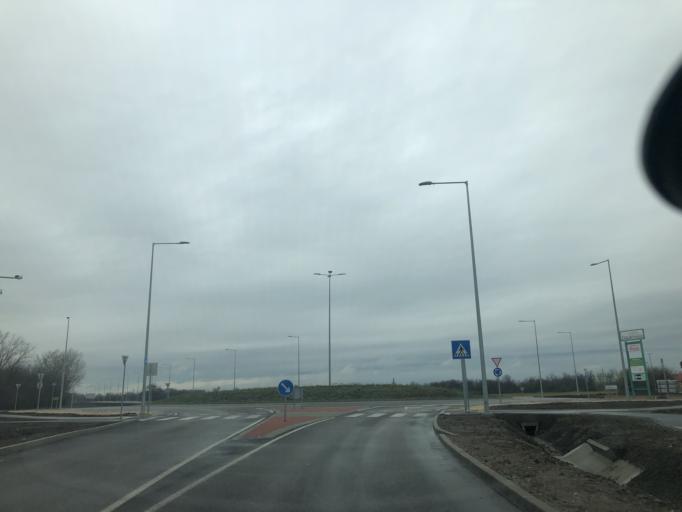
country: HU
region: Gyor-Moson-Sopron
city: Fertod
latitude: 47.6204
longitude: 16.8799
